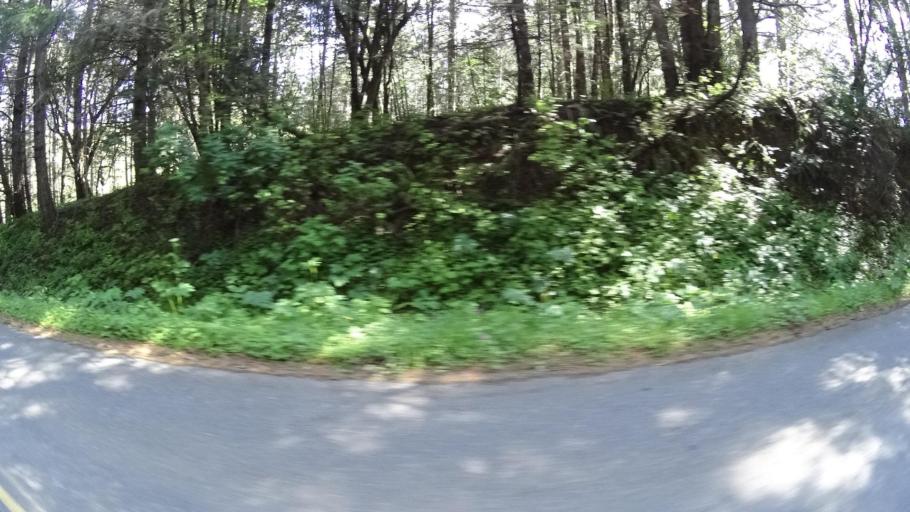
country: US
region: California
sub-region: Humboldt County
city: Ferndale
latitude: 40.3444
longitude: -124.3243
